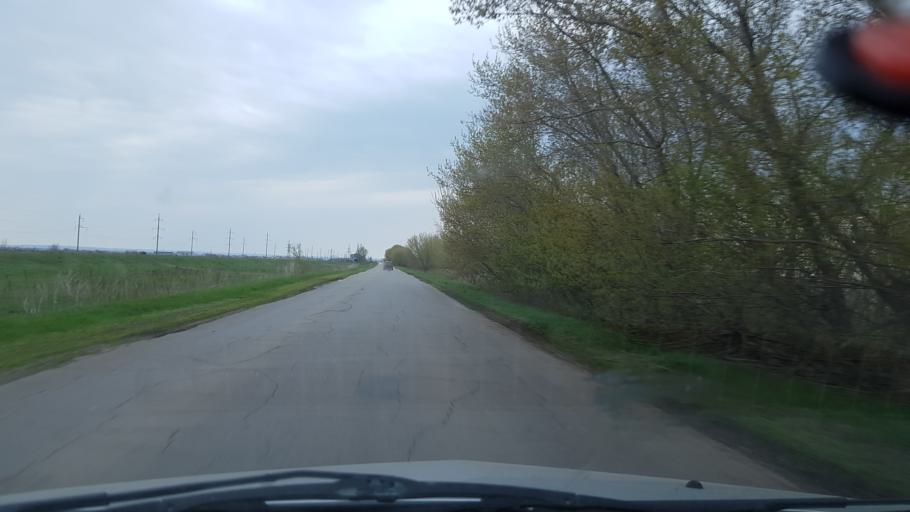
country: RU
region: Samara
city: Khryashchevka
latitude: 53.6698
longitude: 49.1195
